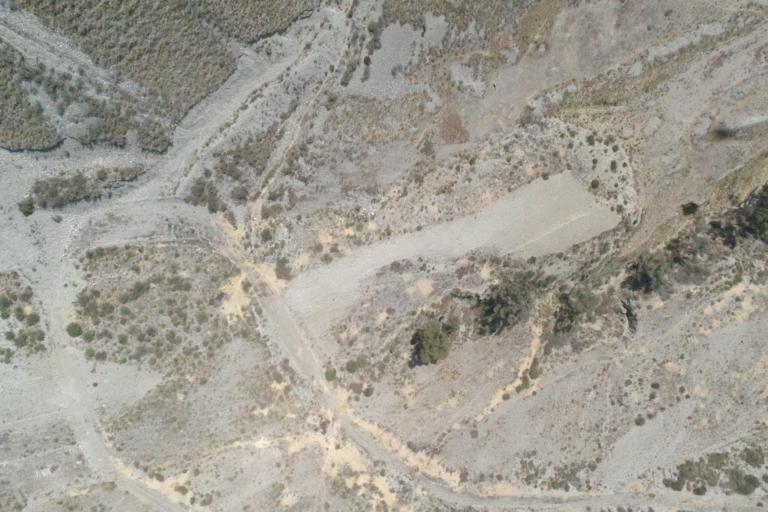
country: BO
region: La Paz
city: La Paz
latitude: -16.4746
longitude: -68.0966
